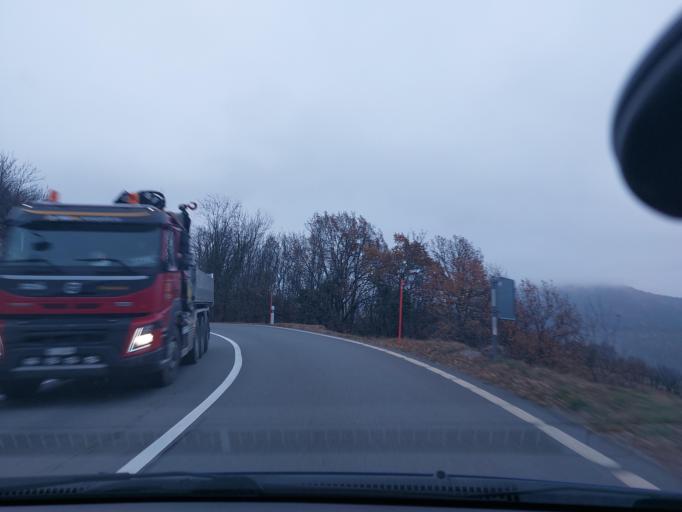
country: CH
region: Valais
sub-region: Sion District
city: Grimisuat
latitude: 46.2658
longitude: 7.3967
